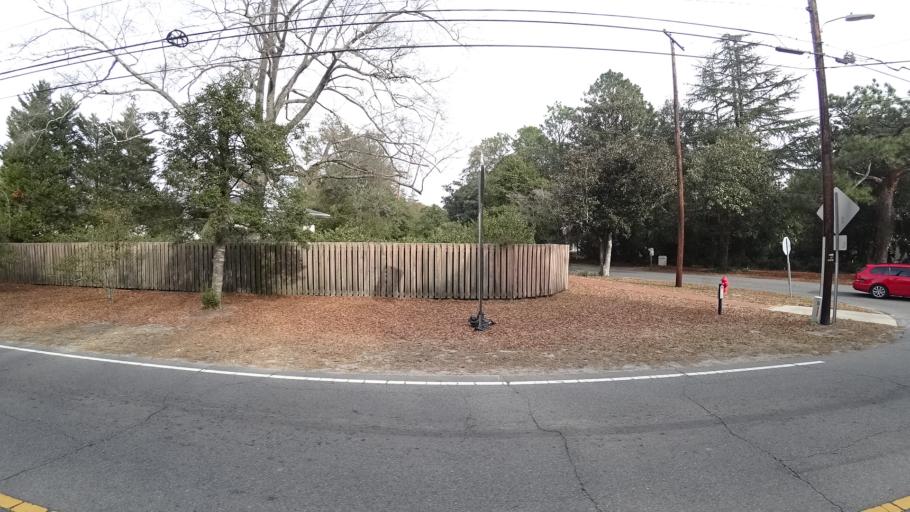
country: US
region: North Carolina
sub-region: Moore County
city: Pinehurst
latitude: 35.1936
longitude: -79.4739
